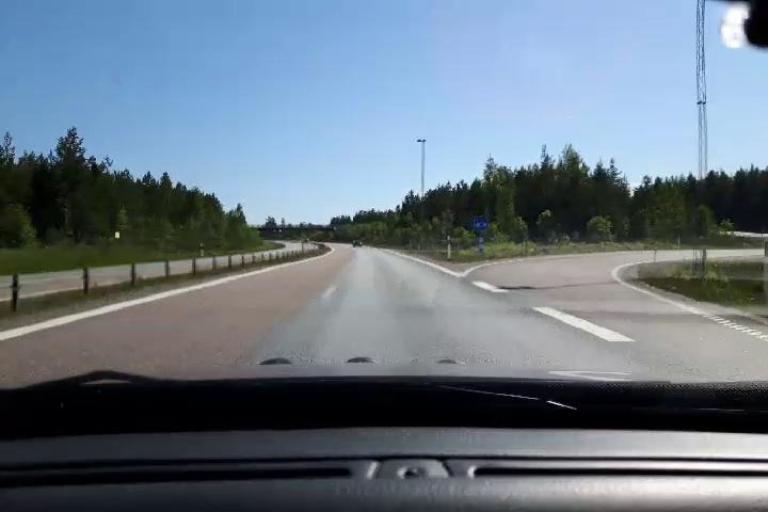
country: SE
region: Gaevleborg
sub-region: Soderhamns Kommun
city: Soderhamn
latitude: 61.3413
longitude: 17.0174
